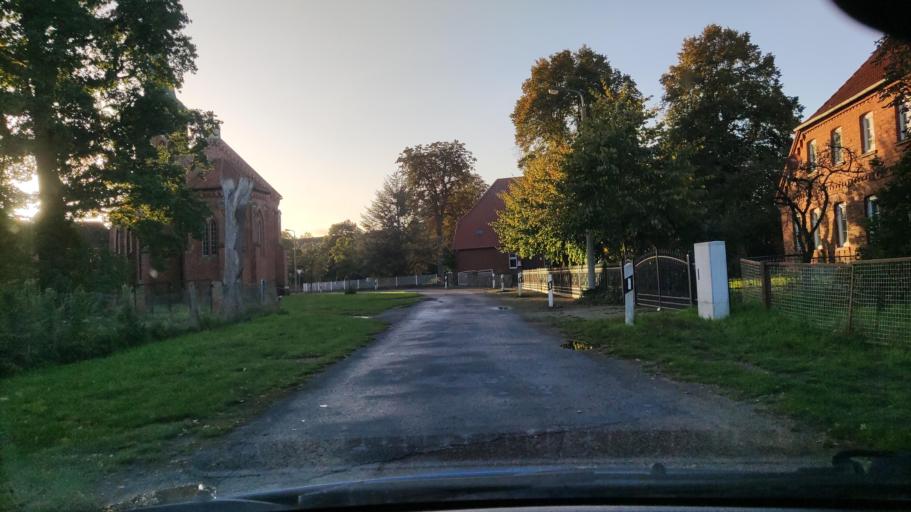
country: DE
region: Lower Saxony
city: Neu Darchau
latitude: 53.3189
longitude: 10.9561
